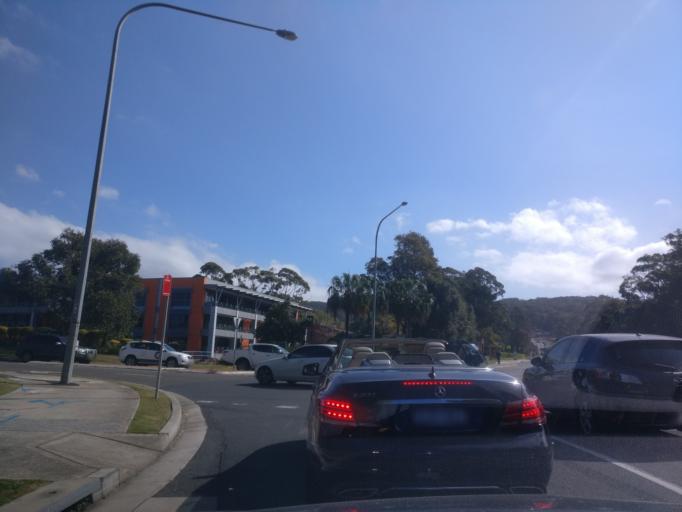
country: AU
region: New South Wales
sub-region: Pittwater
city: Warriewood
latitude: -33.6762
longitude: 151.2900
